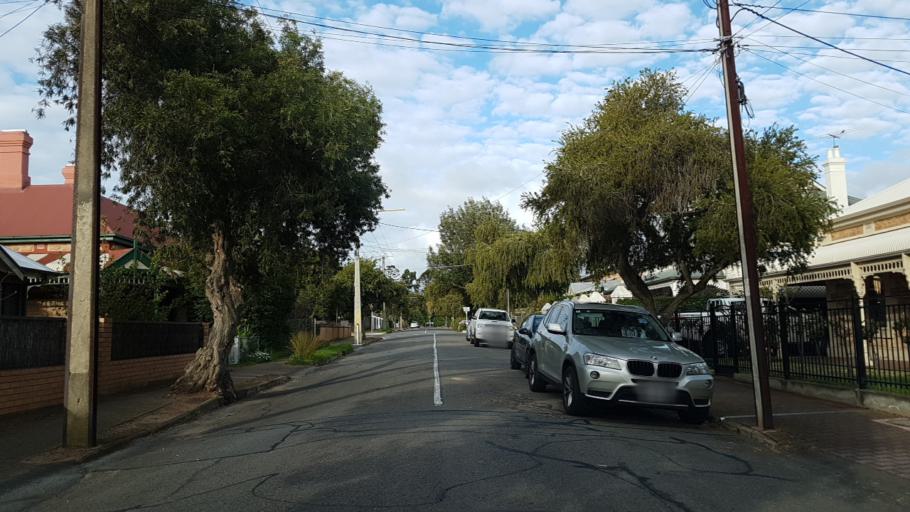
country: AU
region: South Australia
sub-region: Adelaide
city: North Adelaide
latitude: -34.8950
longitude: 138.5914
